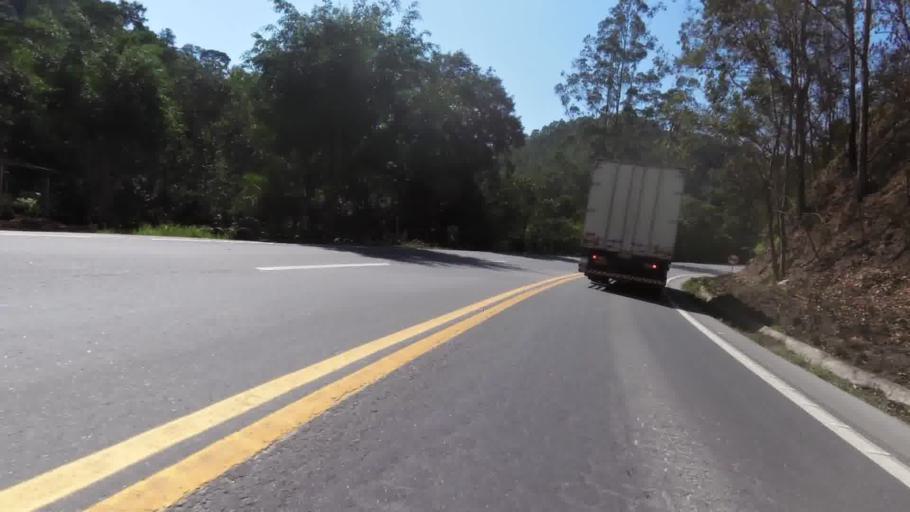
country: BR
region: Espirito Santo
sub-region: Marechal Floriano
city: Marechal Floriano
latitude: -20.4153
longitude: -40.8700
